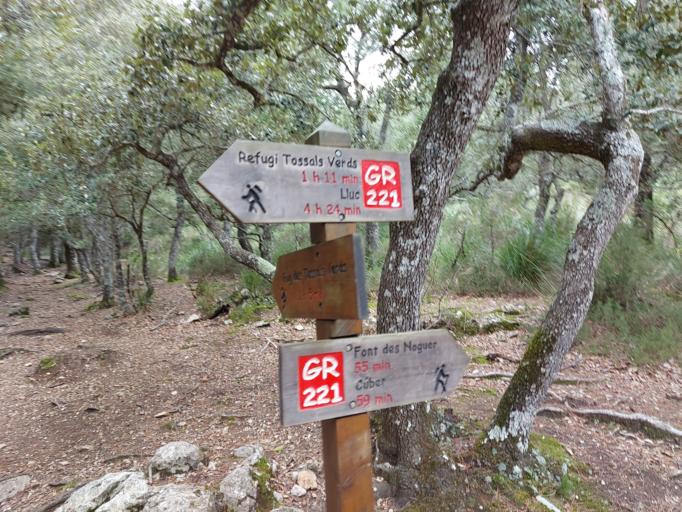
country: ES
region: Balearic Islands
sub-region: Illes Balears
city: Escorca
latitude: 39.7886
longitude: 2.8254
